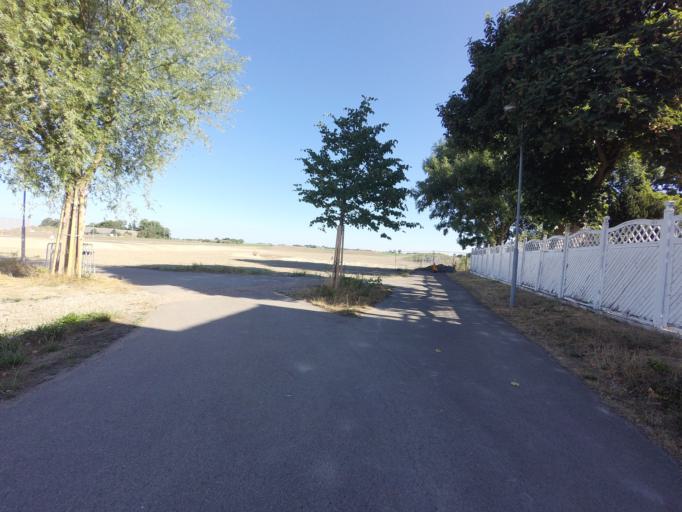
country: SE
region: Skane
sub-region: Trelleborgs Kommun
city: Skare
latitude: 55.4053
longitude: 13.0906
